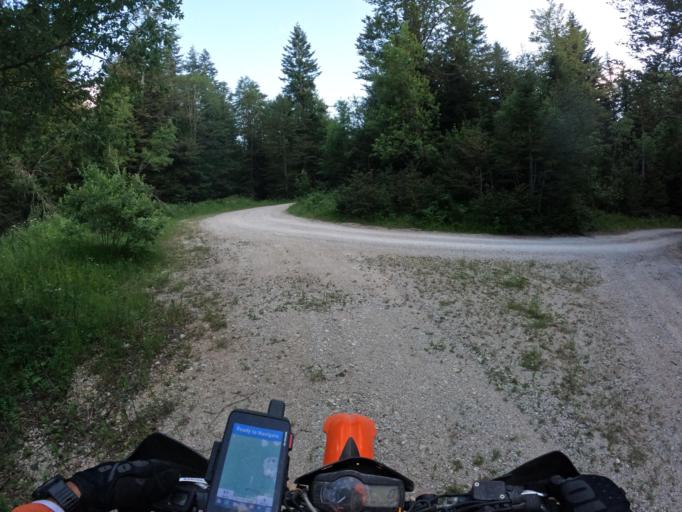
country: BA
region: Federation of Bosnia and Herzegovina
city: Velagici
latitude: 44.3363
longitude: 16.6034
